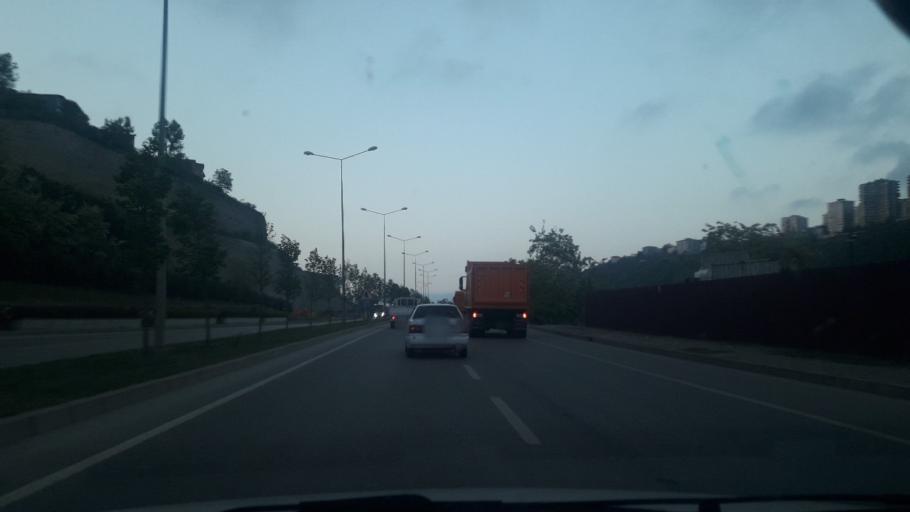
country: TR
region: Samsun
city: Samsun
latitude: 41.3138
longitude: 36.3026
